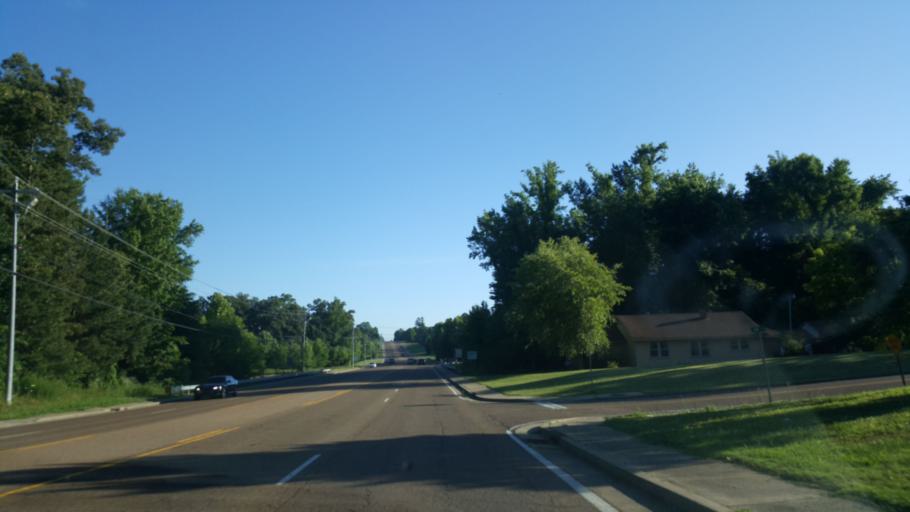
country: US
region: Tennessee
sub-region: Henderson County
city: Lexington
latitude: 35.6668
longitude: -88.3842
